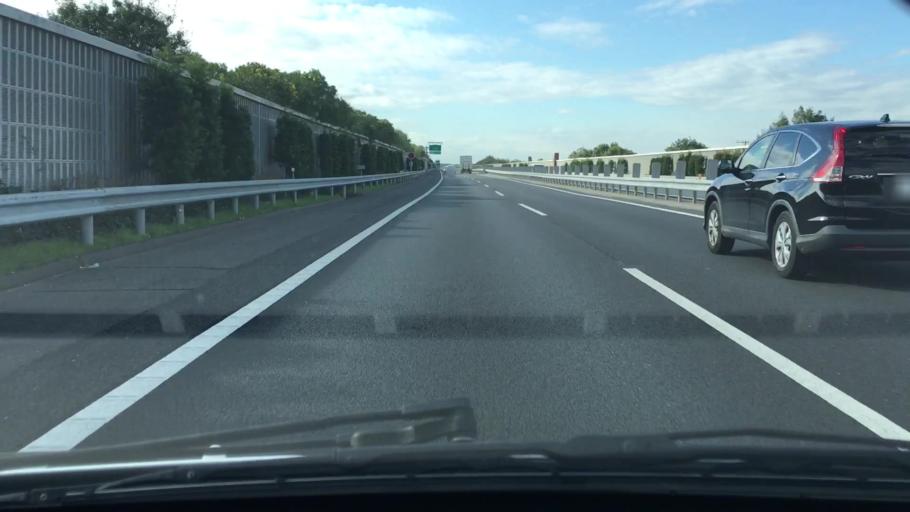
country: JP
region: Chiba
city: Ichihara
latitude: 35.5044
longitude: 140.1027
